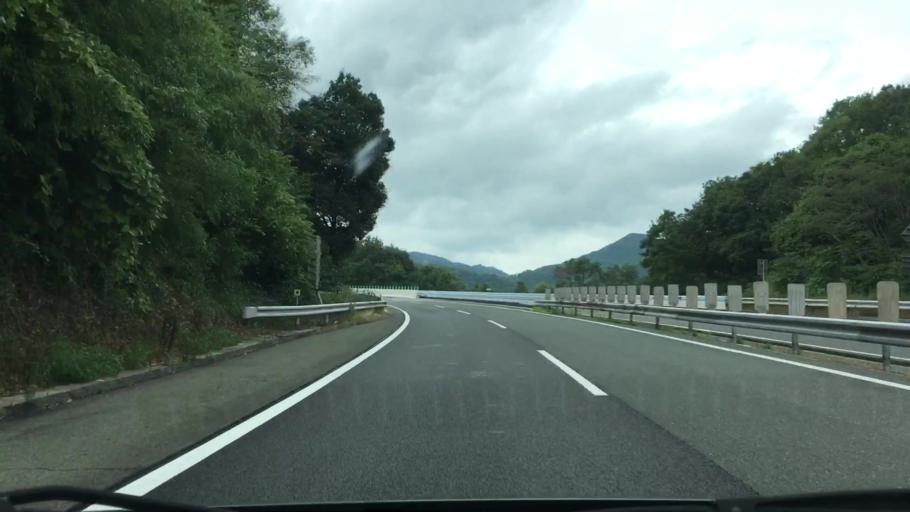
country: JP
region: Hiroshima
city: Shobara
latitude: 34.8959
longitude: 133.2410
